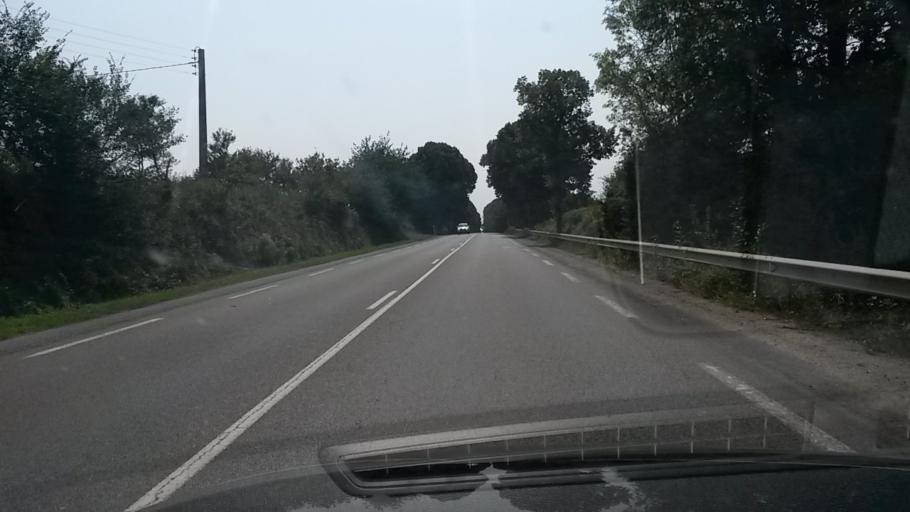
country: FR
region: Pays de la Loire
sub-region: Departement de la Mayenne
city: Chateau-Gontier
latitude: 47.8700
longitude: -0.6878
